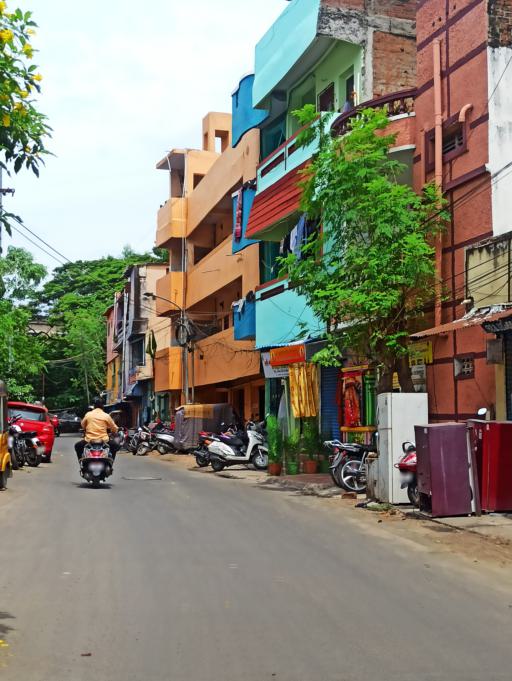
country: IN
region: Tamil Nadu
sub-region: Chennai
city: Chetput
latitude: 13.0580
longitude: 80.2290
